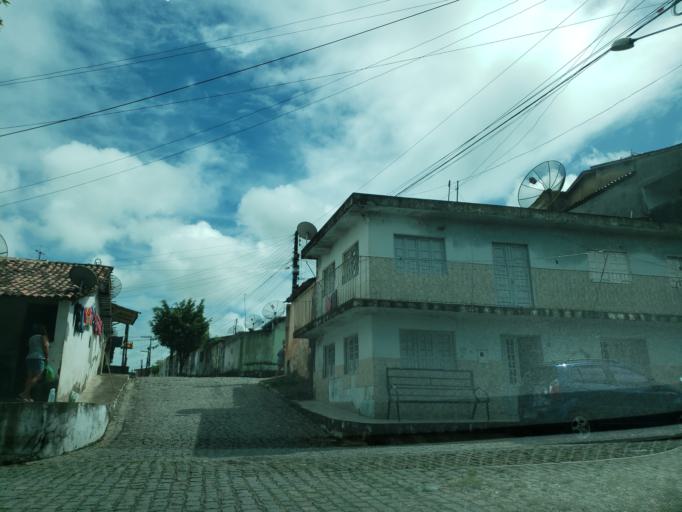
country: BR
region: Alagoas
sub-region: Uniao Dos Palmares
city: Uniao dos Palmares
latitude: -9.1592
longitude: -36.0237
